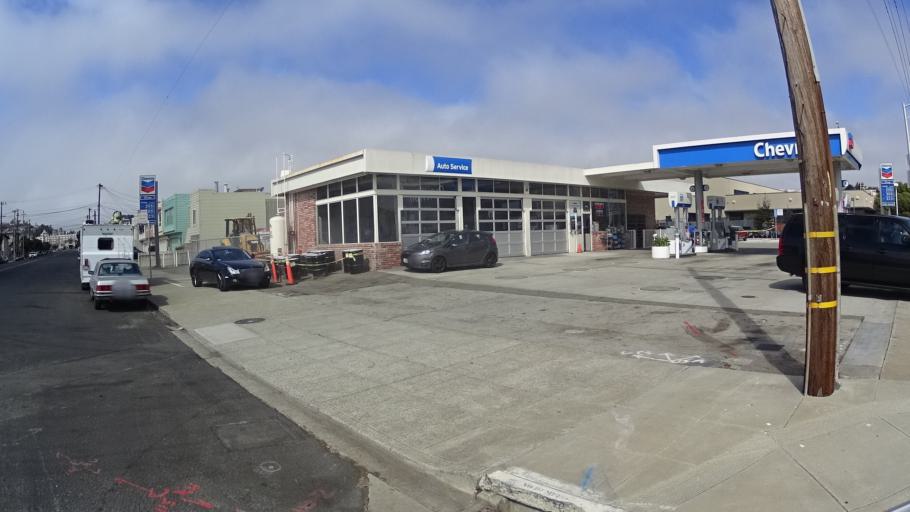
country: US
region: California
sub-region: San Mateo County
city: Brisbane
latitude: 37.7054
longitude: -122.4068
